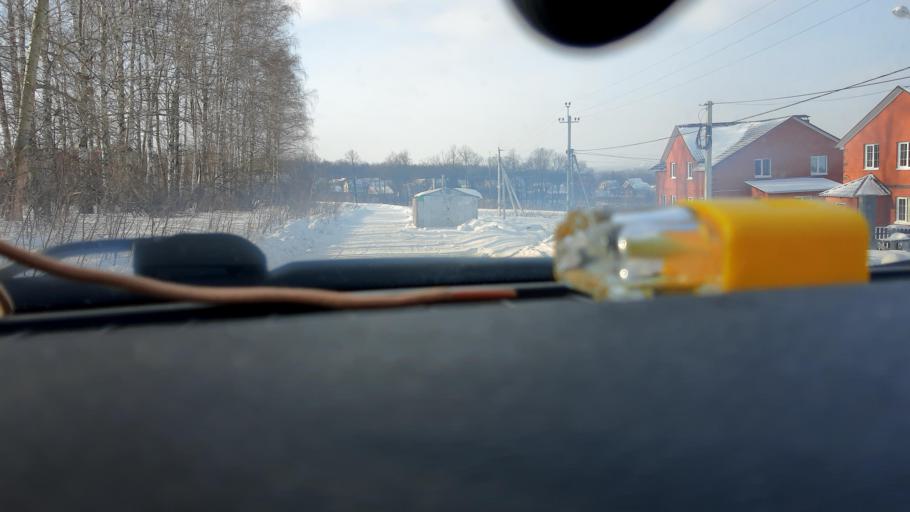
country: RU
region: Bashkortostan
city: Kabakovo
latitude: 54.6296
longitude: 56.0656
